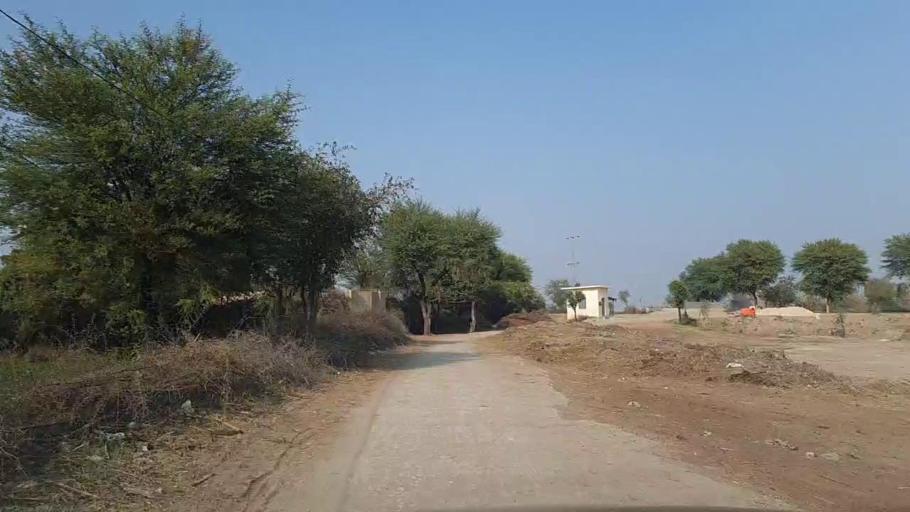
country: PK
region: Sindh
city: Daur
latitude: 26.4306
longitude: 68.4091
